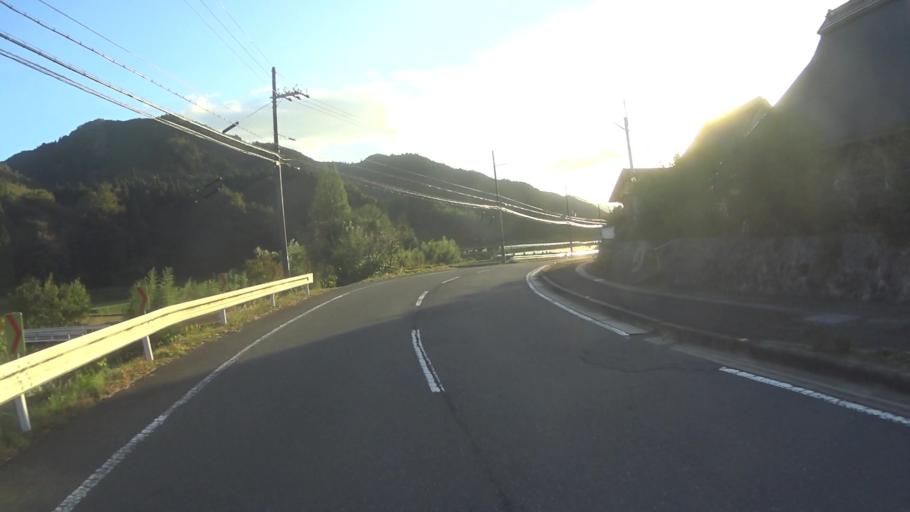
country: JP
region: Kyoto
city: Ayabe
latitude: 35.2330
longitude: 135.2539
